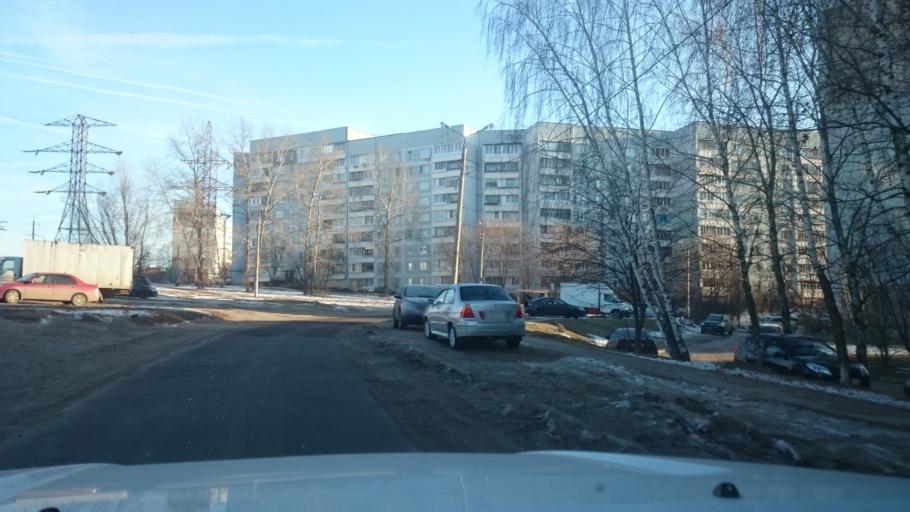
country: RU
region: Tula
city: Tula
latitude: 54.2137
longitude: 37.6885
